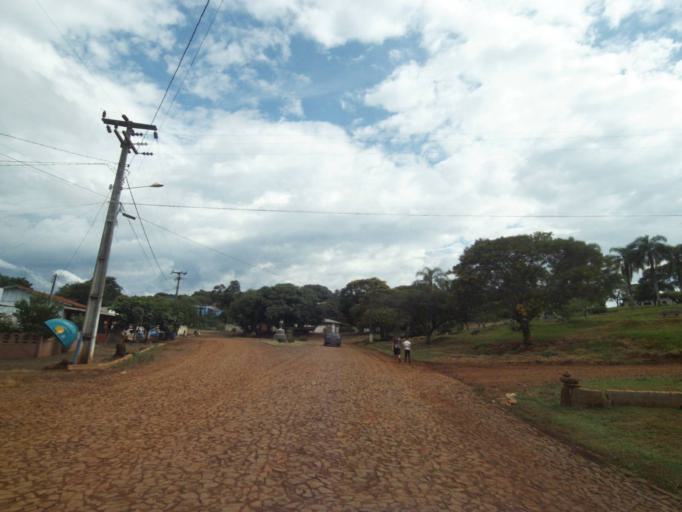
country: BR
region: Parana
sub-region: Pitanga
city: Pitanga
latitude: -24.9079
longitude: -52.0334
